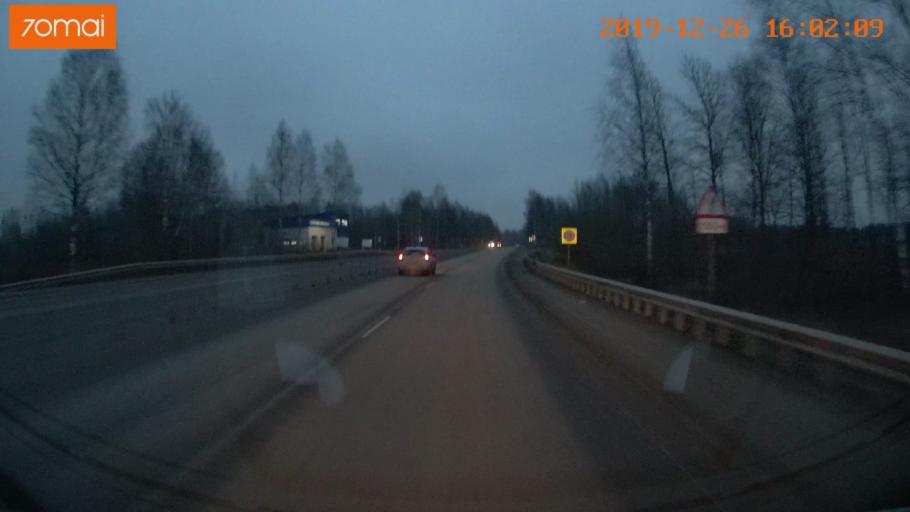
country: RU
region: Jaroslavl
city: Rybinsk
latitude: 58.0138
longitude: 38.8300
